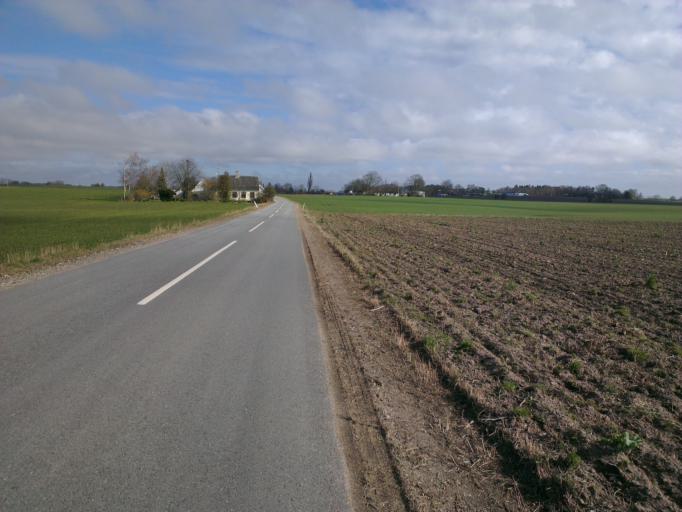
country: DK
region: Capital Region
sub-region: Frederikssund Kommune
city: Frederikssund
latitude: 55.8660
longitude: 12.1136
